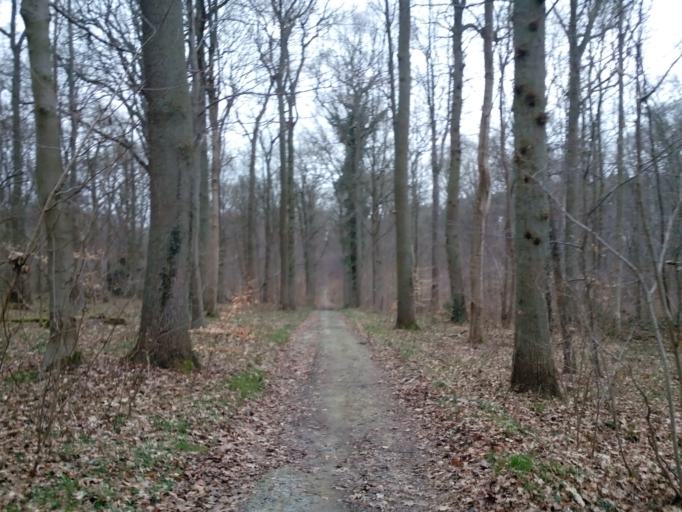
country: BE
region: Flanders
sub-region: Provincie Vlaams-Brabant
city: Bierbeek
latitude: 50.7999
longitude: 4.7203
